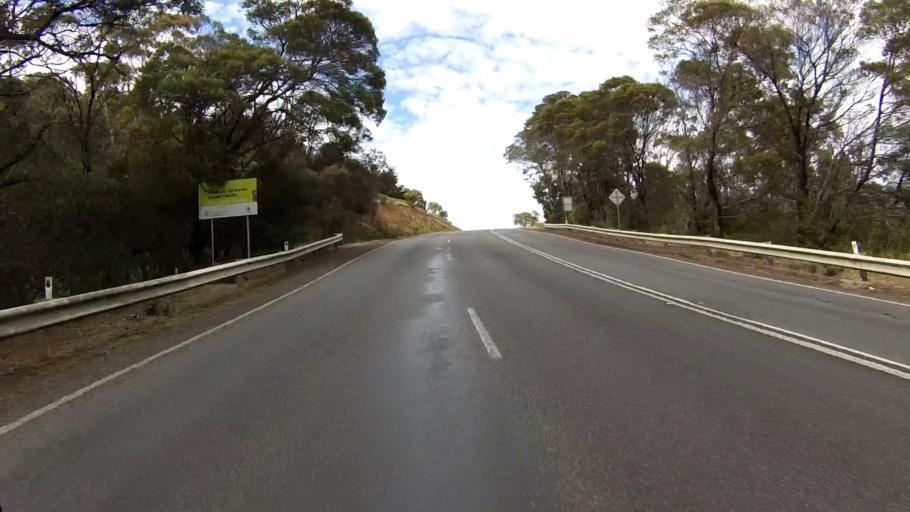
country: AU
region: Tasmania
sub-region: Brighton
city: Old Beach
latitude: -42.7907
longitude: 147.2932
